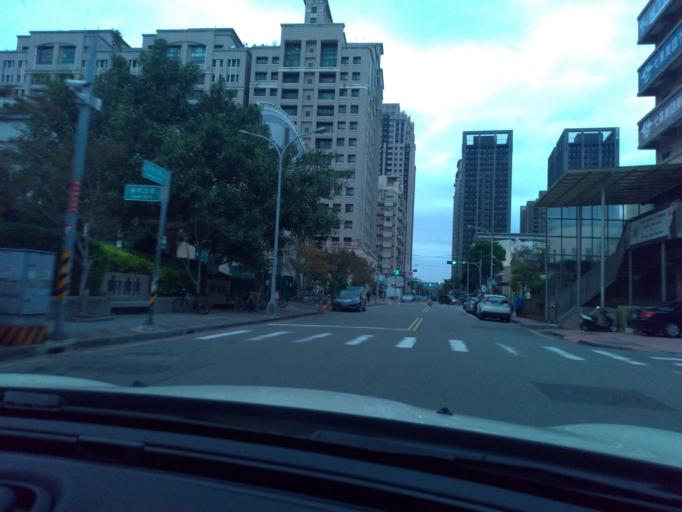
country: TW
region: Taiwan
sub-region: Hsinchu
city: Zhubei
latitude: 24.8235
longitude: 121.0256
